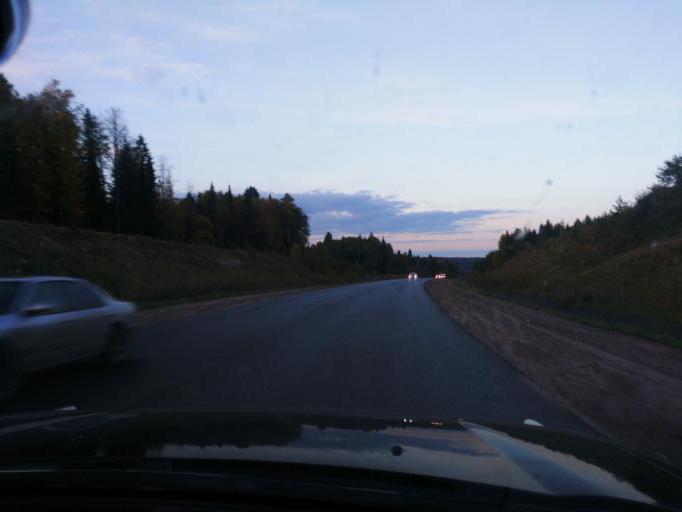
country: RU
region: Perm
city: Polazna
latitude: 58.2793
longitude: 56.4299
